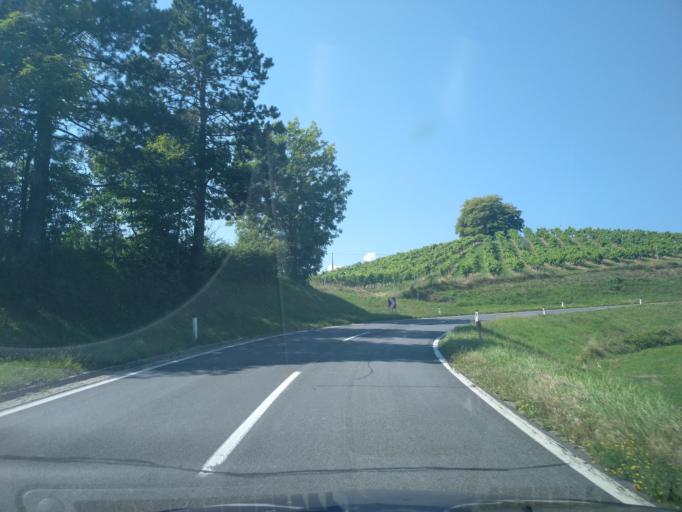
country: AT
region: Styria
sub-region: Politischer Bezirk Leibnitz
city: Leutschach
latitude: 46.6783
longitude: 15.4793
